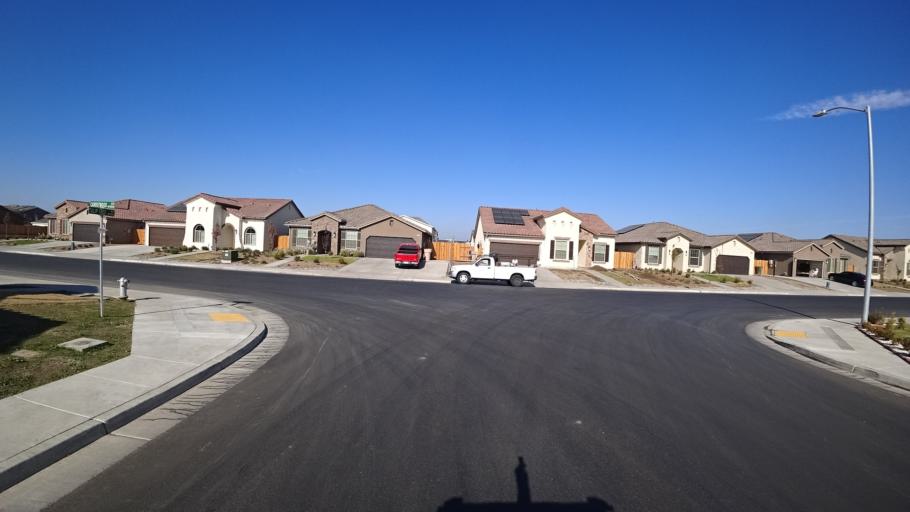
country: US
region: California
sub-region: Kern County
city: Greenfield
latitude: 35.2908
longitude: -119.0676
